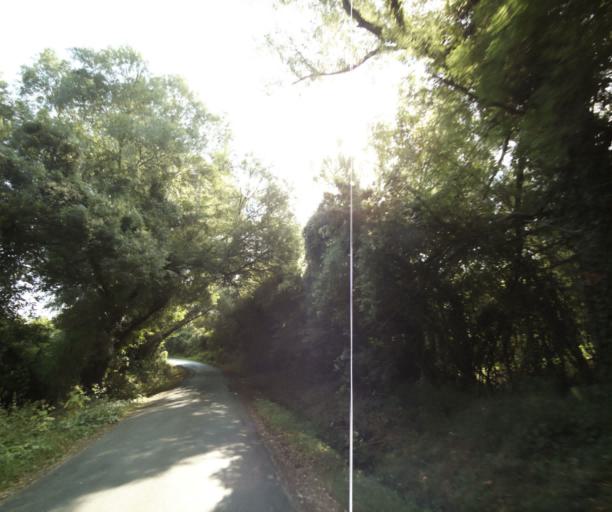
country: FR
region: Poitou-Charentes
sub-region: Departement de la Charente-Maritime
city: Tonnay-Charente
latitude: 45.9642
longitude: -0.8589
